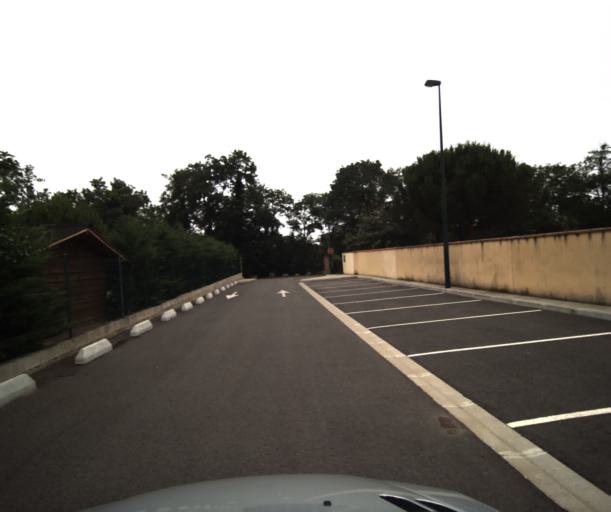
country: FR
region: Midi-Pyrenees
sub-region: Departement de la Haute-Garonne
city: Pinsaguel
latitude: 43.5113
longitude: 1.3900
